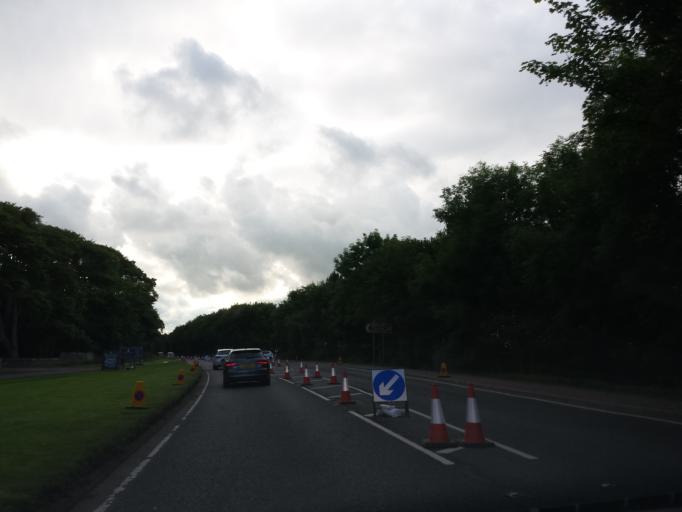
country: GB
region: Scotland
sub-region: Fife
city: Saint Andrews
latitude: 56.3474
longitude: -2.8217
